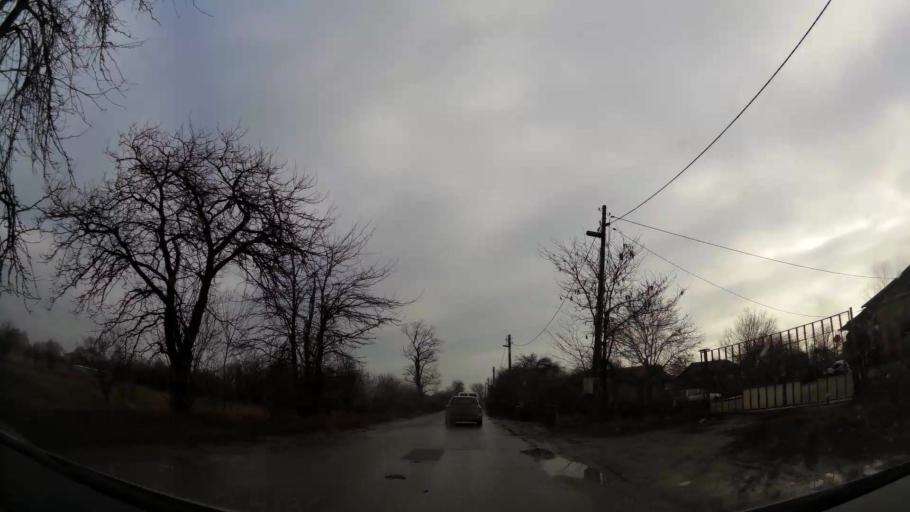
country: BG
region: Sofia-Capital
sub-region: Stolichna Obshtina
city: Sofia
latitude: 42.7236
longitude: 23.3698
